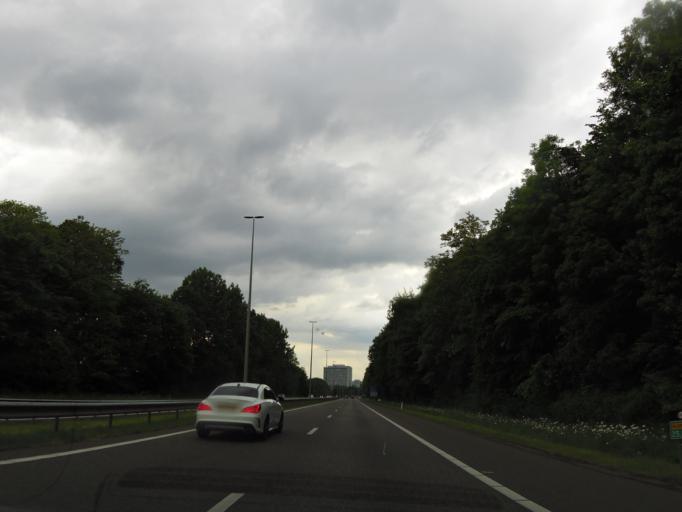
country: NL
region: Limburg
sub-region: Gemeente Heerlen
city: Heerlen
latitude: 50.8624
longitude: 5.9913
